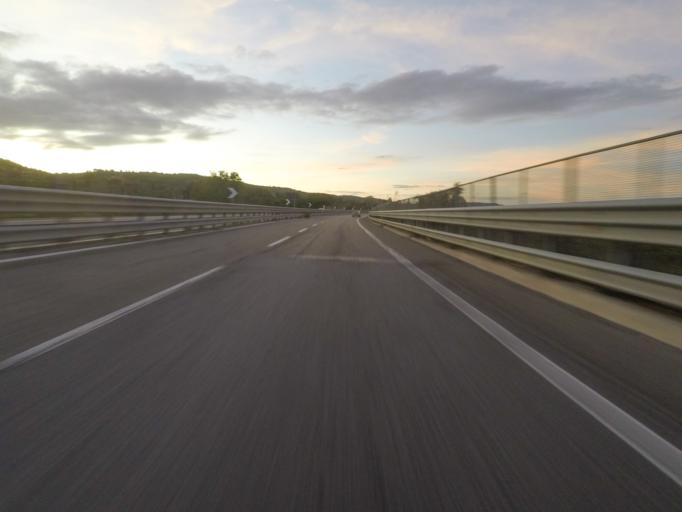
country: IT
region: Tuscany
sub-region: Provincia di Siena
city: Sinalunga
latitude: 43.2294
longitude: 11.7329
